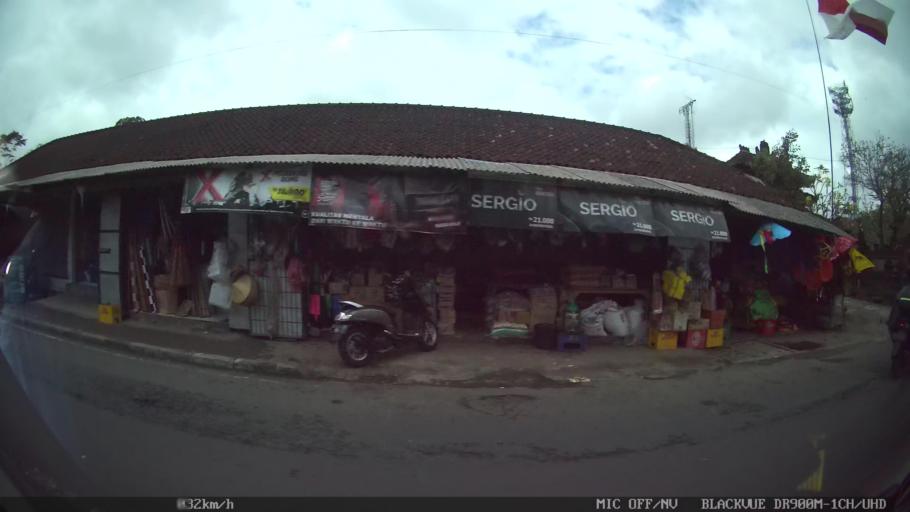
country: ID
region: Bali
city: Banjar Bucu
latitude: -8.5870
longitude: 115.2089
